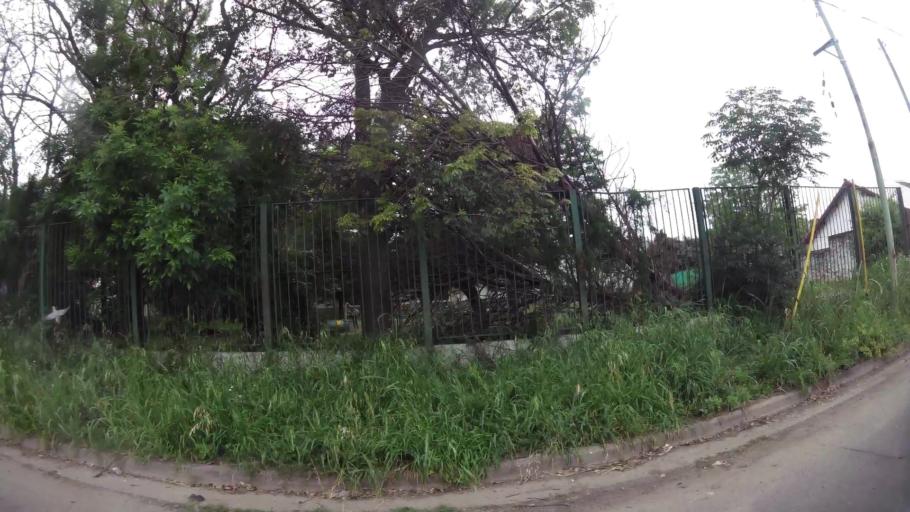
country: AR
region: Buenos Aires
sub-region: Partido de Zarate
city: Zarate
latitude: -34.1147
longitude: -59.0172
